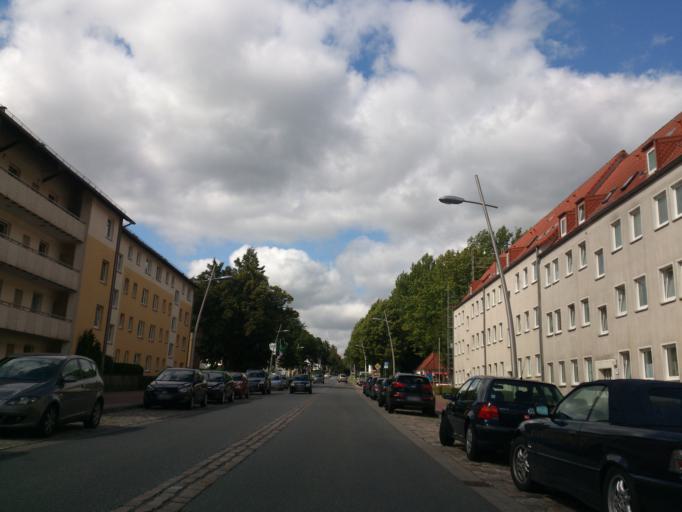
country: DE
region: Schleswig-Holstein
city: Flensburg
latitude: 54.8072
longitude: 9.4229
